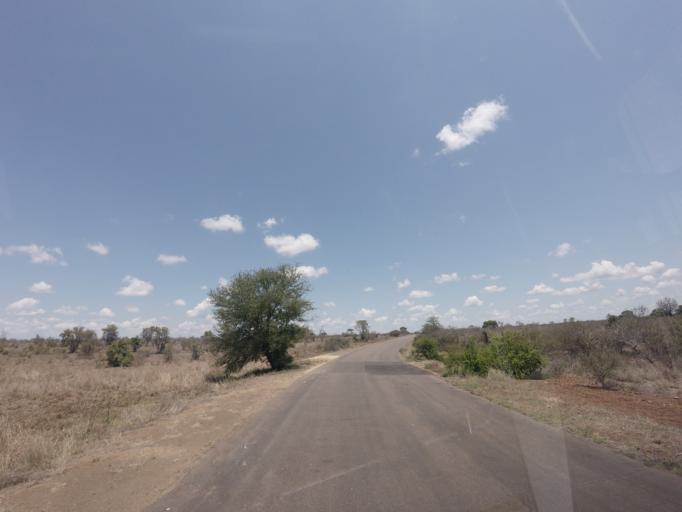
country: ZA
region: Mpumalanga
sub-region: Ehlanzeni District
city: Komatipoort
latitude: -24.7980
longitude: 31.8648
